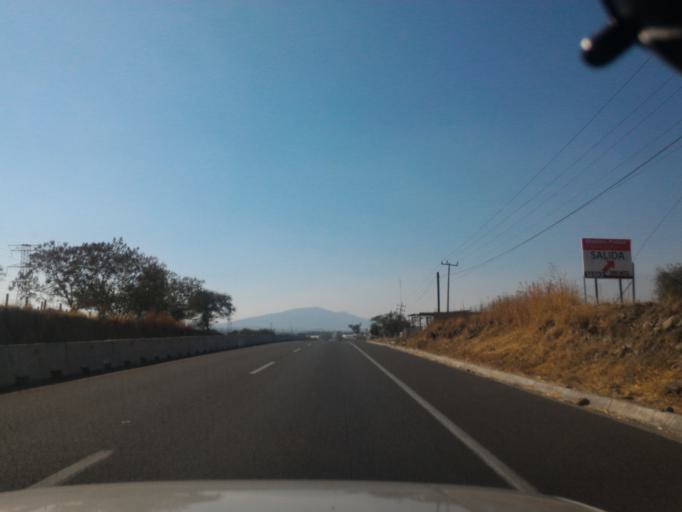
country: MX
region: Jalisco
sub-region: Poncitlan
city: Santa Cruz el Grande
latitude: 20.3654
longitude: -102.8273
